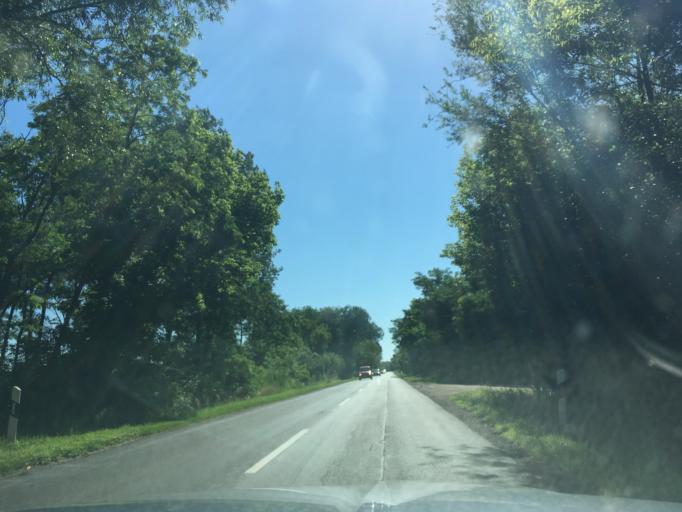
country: HU
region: Hajdu-Bihar
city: Hajdusamson
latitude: 47.5255
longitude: 21.7523
